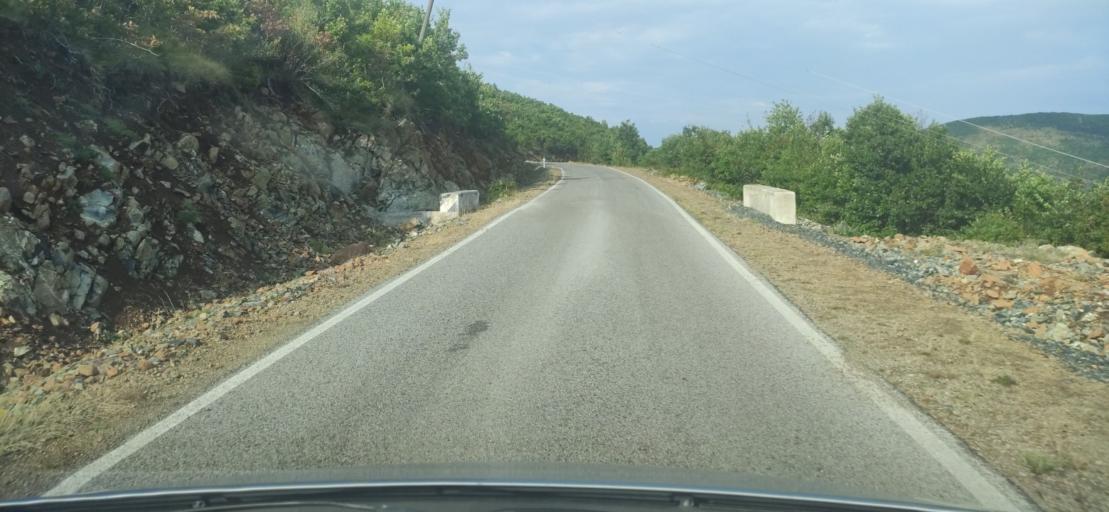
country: AL
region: Shkoder
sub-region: Rrethi i Pukes
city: Iballe
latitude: 42.1753
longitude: 19.9995
